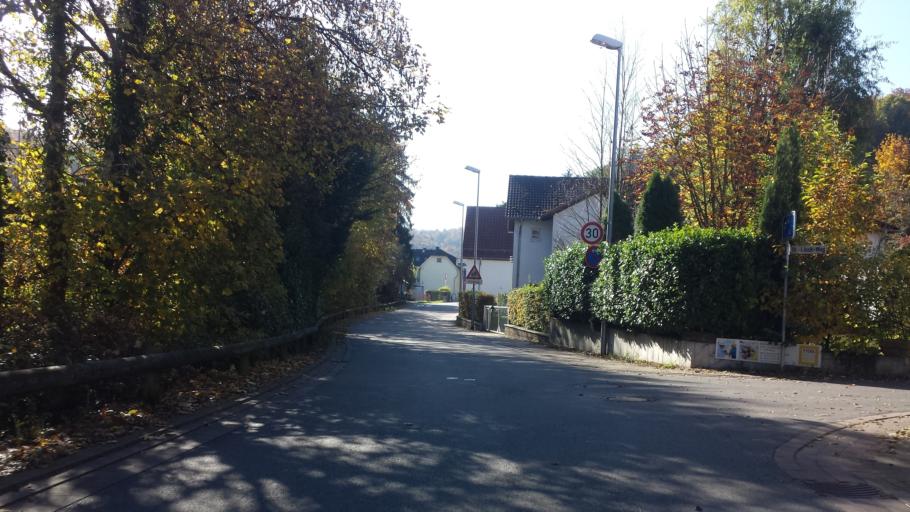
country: DE
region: Hesse
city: Zwingenberg
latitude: 49.7105
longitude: 8.6487
